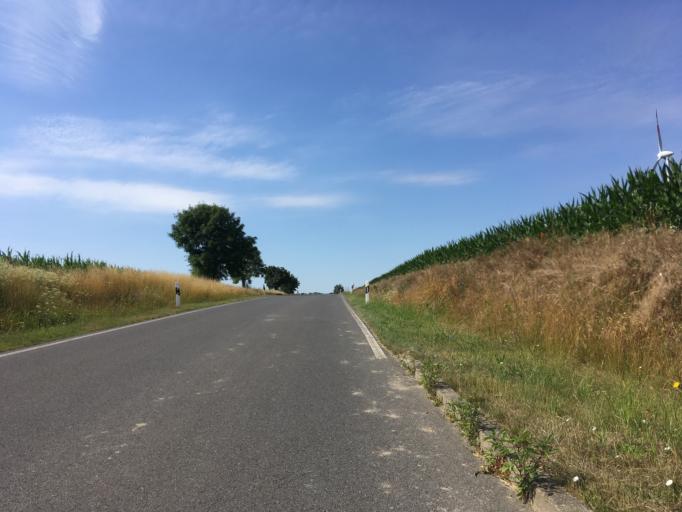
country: DE
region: Brandenburg
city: Gramzow
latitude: 53.2686
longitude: 14.0695
